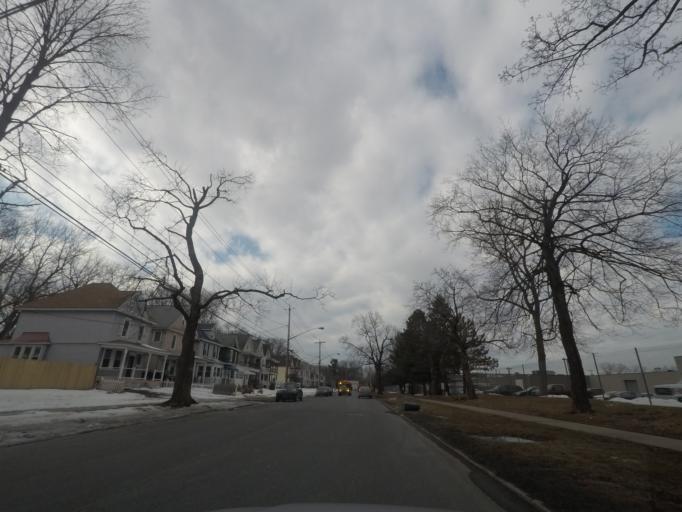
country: US
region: New York
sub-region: Albany County
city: West Albany
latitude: 42.6727
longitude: -73.7739
